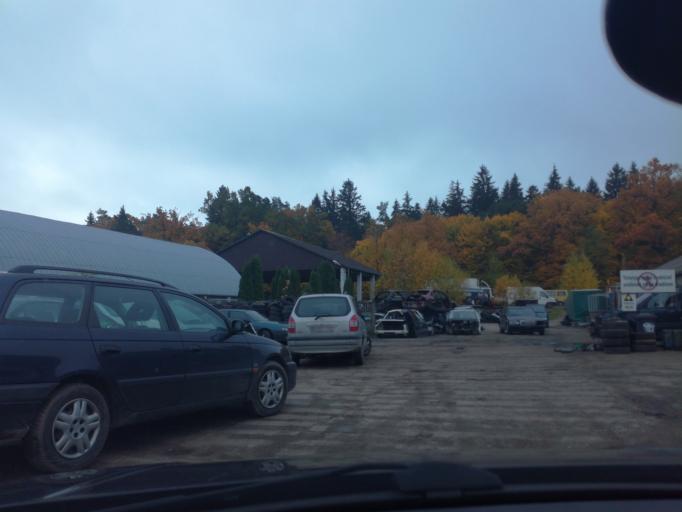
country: LT
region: Alytaus apskritis
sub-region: Alytus
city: Alytus
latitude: 54.3859
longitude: 24.0356
